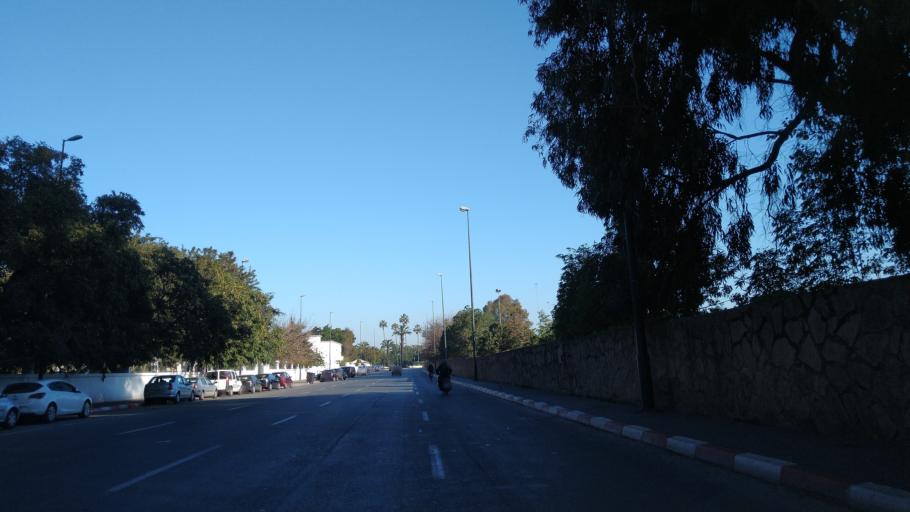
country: MA
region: Rabat-Sale-Zemmour-Zaer
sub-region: Rabat
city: Rabat
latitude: 34.0049
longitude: -6.8425
